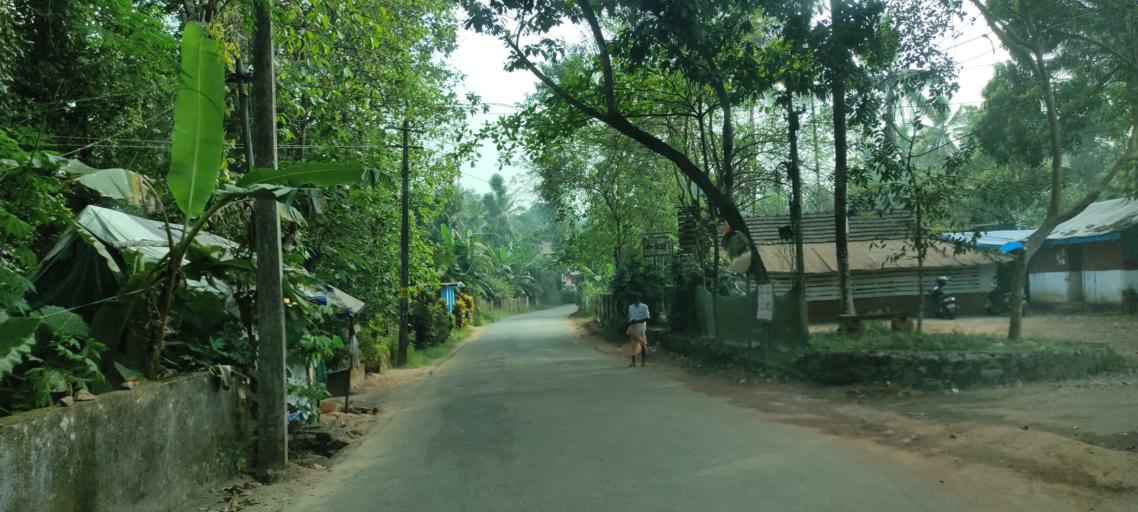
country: IN
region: Kerala
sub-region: Ernakulam
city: Piravam
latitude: 9.7889
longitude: 76.4985
